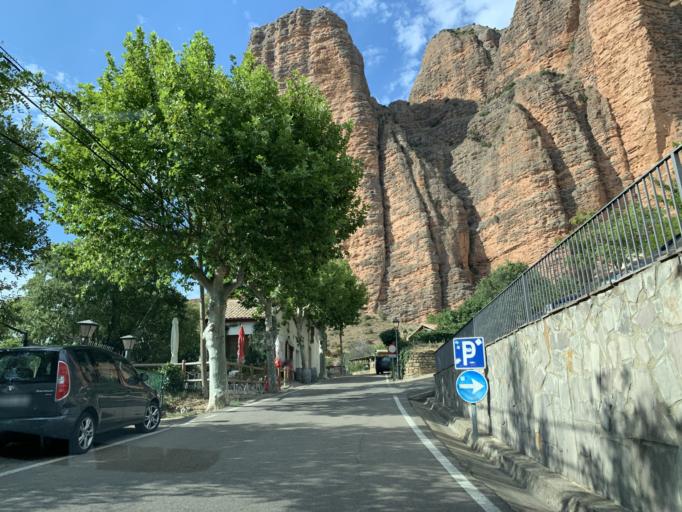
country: ES
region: Aragon
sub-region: Provincia de Zaragoza
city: Santa Eulalia de Gallego
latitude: 42.3476
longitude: -0.7272
